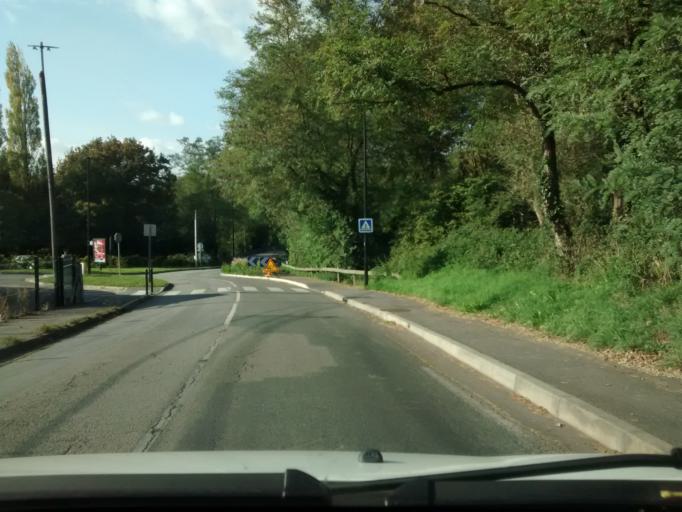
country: FR
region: Pays de la Loire
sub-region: Departement de la Loire-Atlantique
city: Sautron
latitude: 47.2679
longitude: -1.6704
